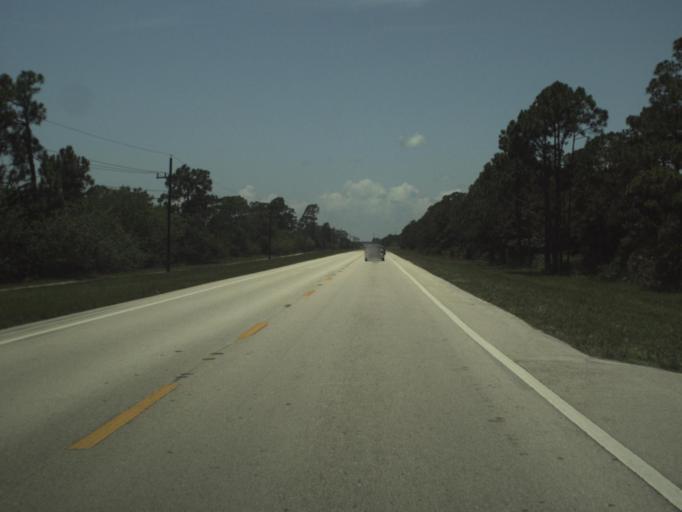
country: US
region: Florida
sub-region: Martin County
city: Palm City
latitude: 27.1618
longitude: -80.3704
